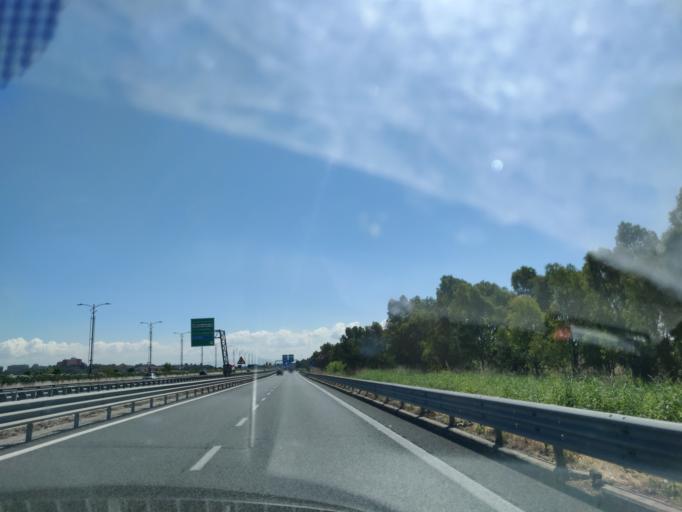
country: IT
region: Latium
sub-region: Citta metropolitana di Roma Capitale
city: Ponte Galeria-La Pisana
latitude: 41.8163
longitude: 12.3707
